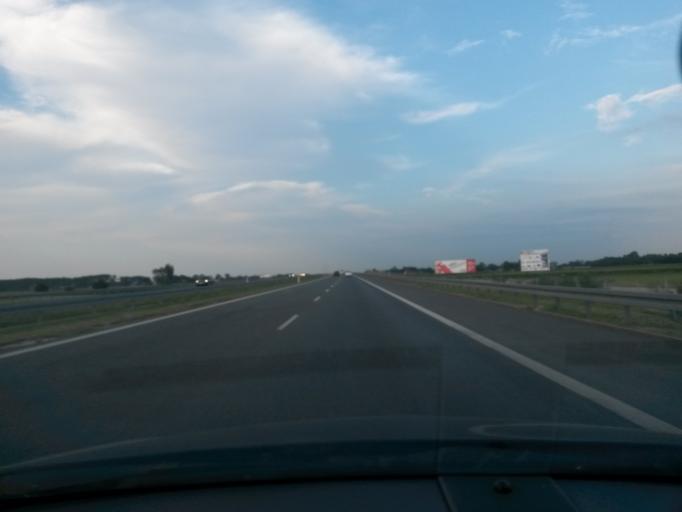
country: PL
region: Masovian Voivodeship
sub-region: Powiat warszawski zachodni
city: Bieniewice
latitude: 52.1237
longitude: 20.5246
